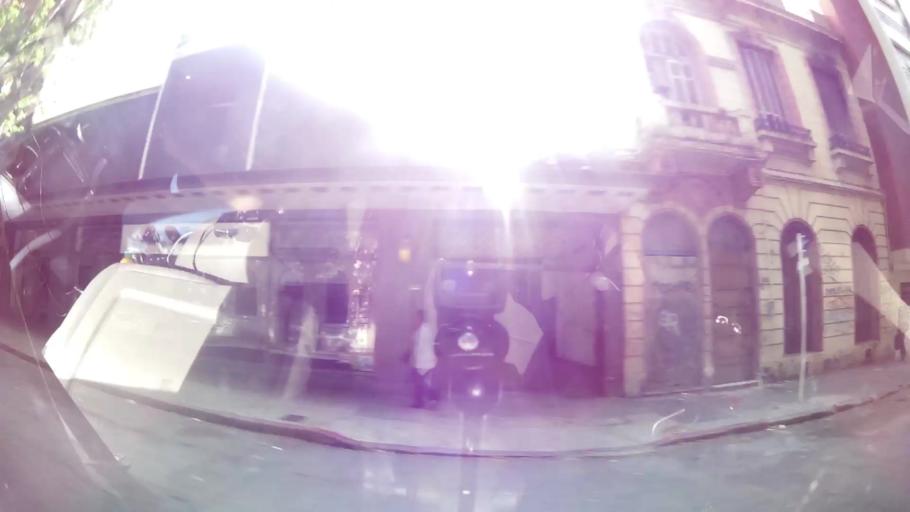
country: UY
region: Montevideo
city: Montevideo
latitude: -34.9074
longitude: -56.1923
